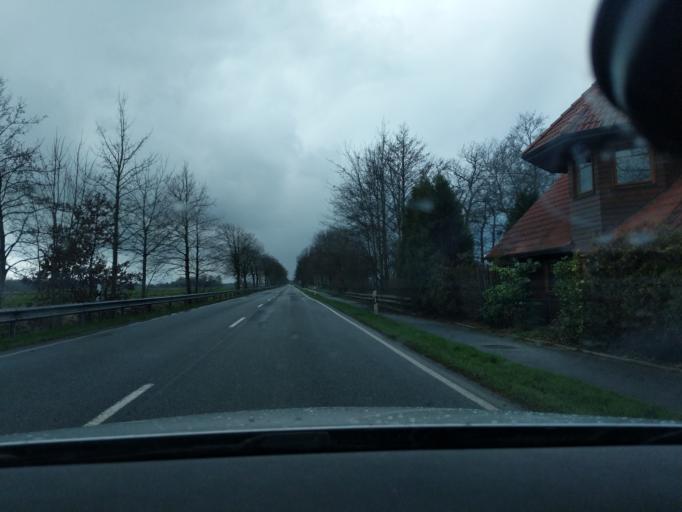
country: DE
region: Lower Saxony
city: Osten
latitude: 53.7206
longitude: 9.2383
